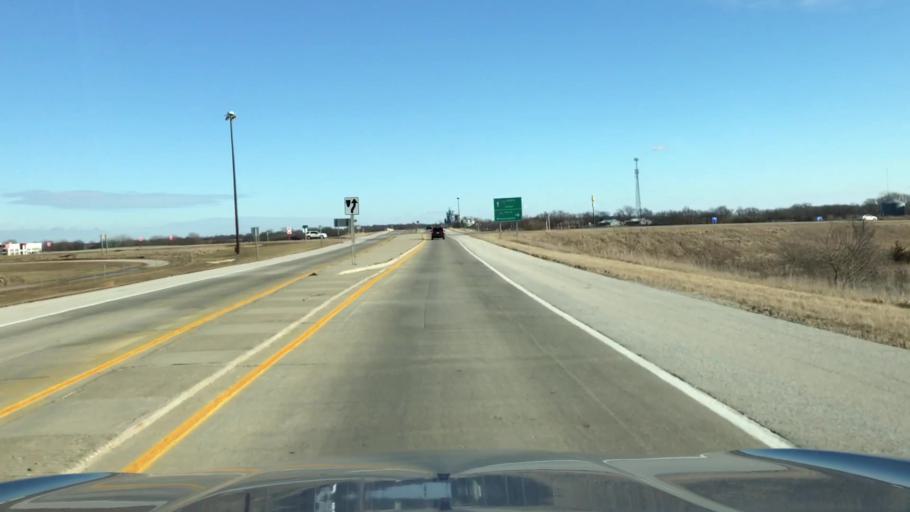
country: US
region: Illinois
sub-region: McLean County
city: Lexington
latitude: 40.6452
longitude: -88.8135
